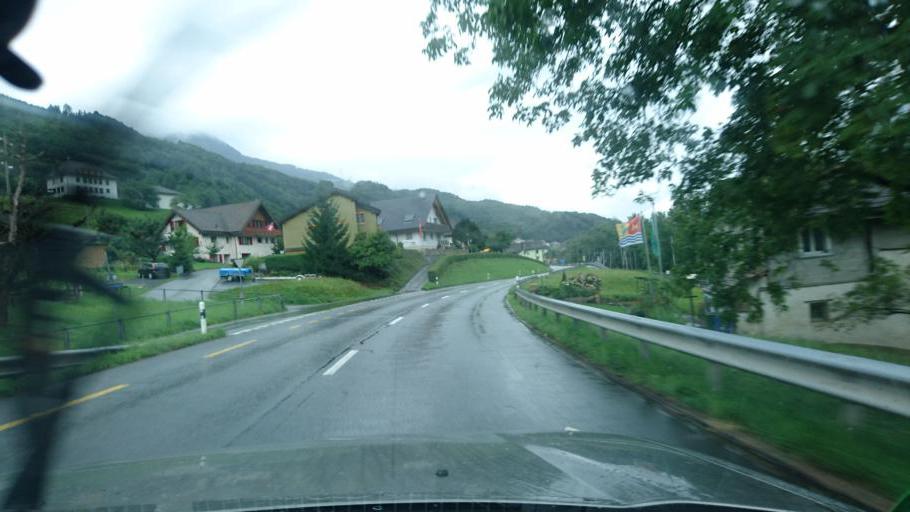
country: CH
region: Saint Gallen
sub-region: Wahlkreis Sarganserland
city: Walenstadt
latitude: 47.1132
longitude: 9.2865
